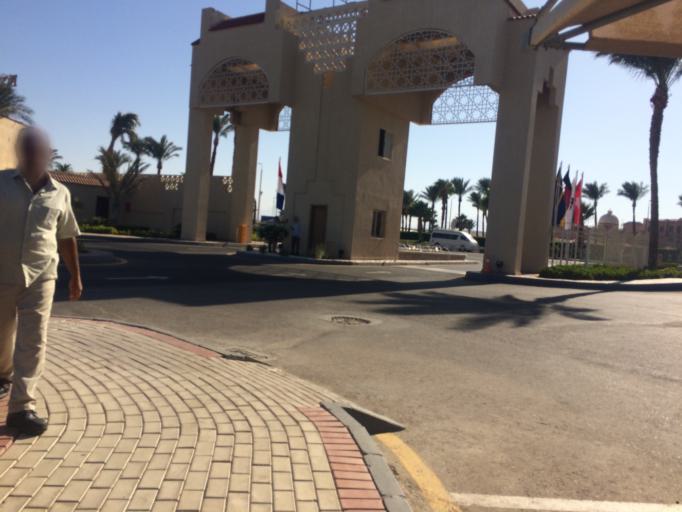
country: EG
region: Red Sea
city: Hurghada
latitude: 27.1222
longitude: 33.8247
